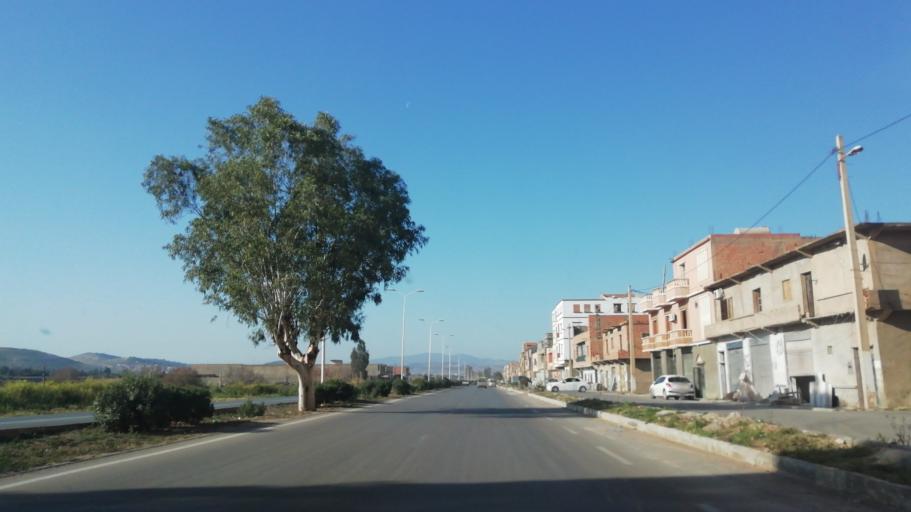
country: DZ
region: Mascara
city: Mascara
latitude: 35.6160
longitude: 0.1064
